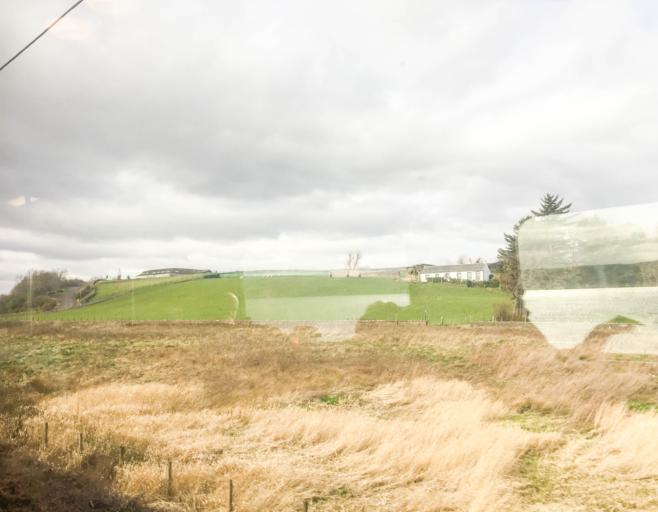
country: GB
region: Scotland
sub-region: Argyll and Bute
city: Cardross
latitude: 55.9518
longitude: -4.6257
